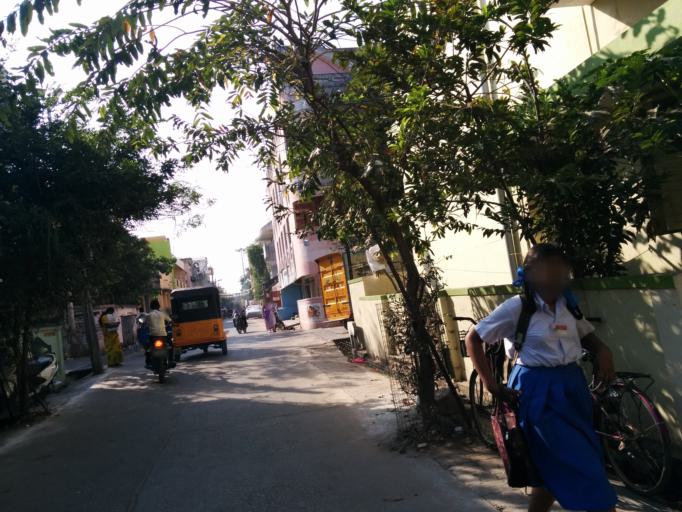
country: IN
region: Pondicherry
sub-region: Puducherry
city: Puducherry
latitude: 11.9511
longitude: 79.8336
